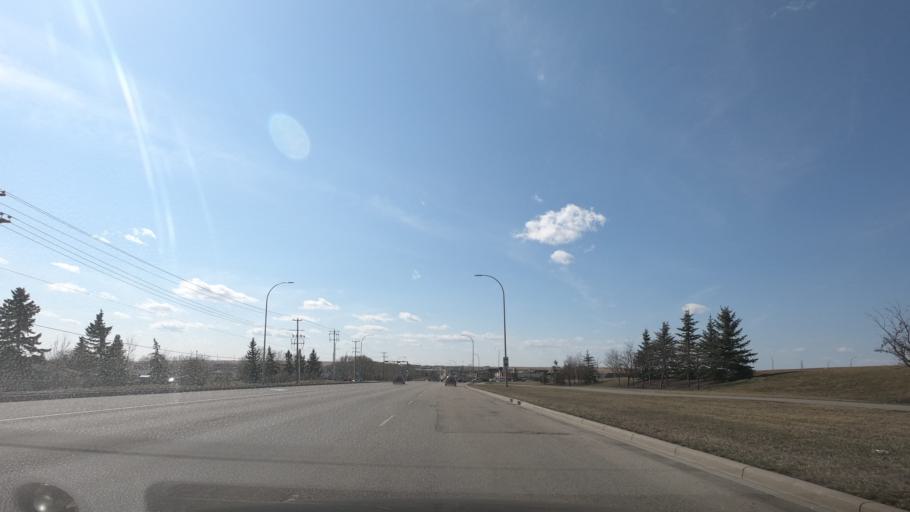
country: CA
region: Alberta
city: Airdrie
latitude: 51.3001
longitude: -114.0107
